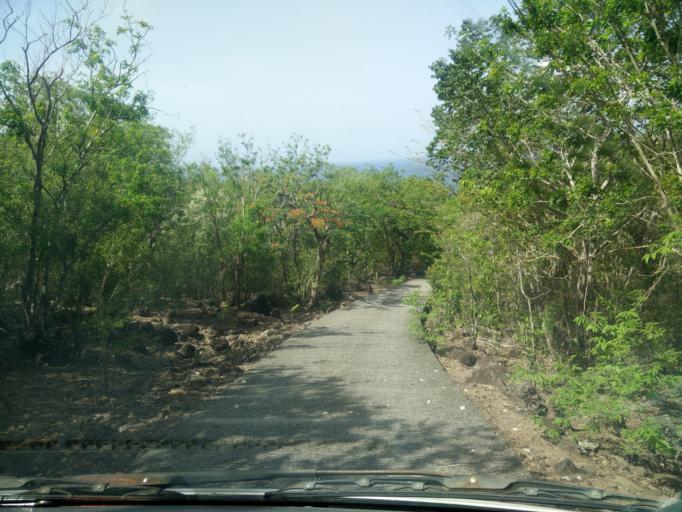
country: GP
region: Guadeloupe
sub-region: Guadeloupe
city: Terre-de-Bas
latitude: 15.8539
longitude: -61.6259
